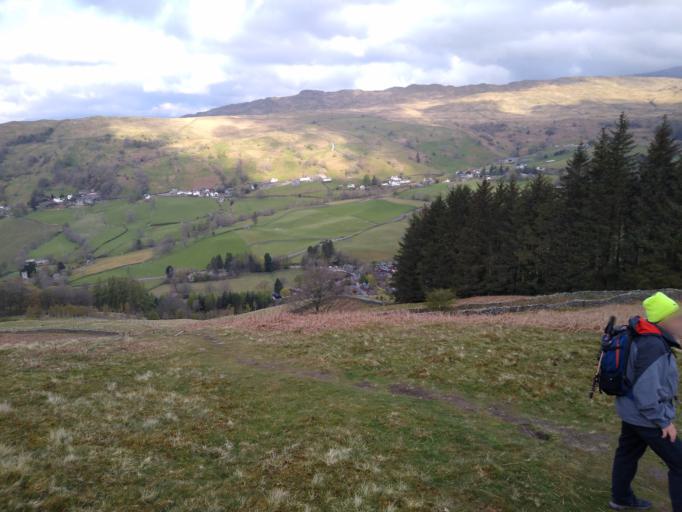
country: GB
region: England
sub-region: Cumbria
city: Windermere
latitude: 54.4174
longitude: -2.8950
